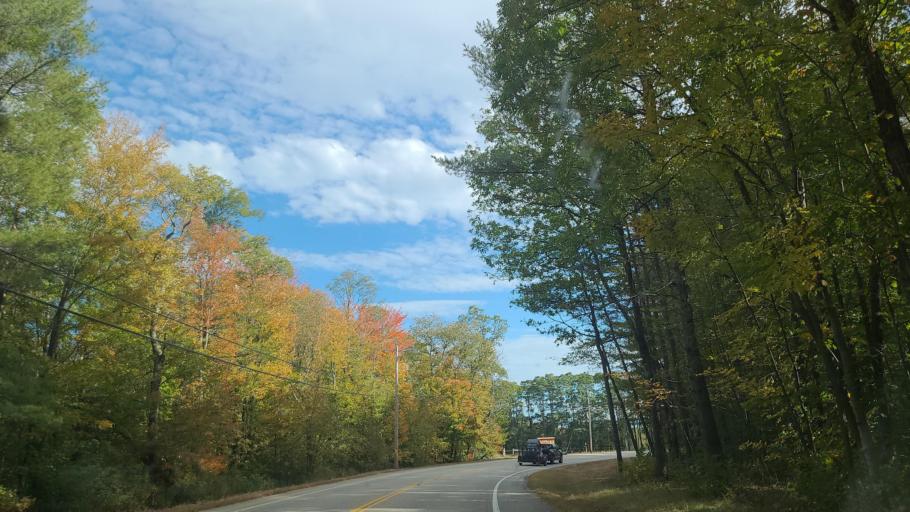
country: US
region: New Hampshire
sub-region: Carroll County
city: Conway
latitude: 43.9988
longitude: -71.1233
